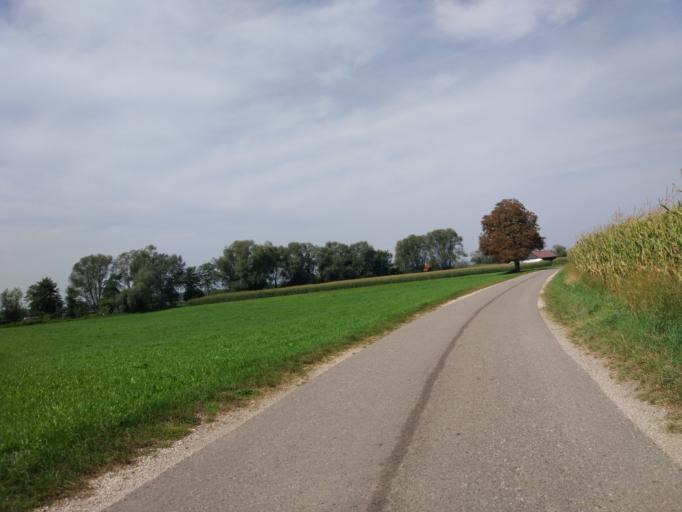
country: DE
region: Baden-Wuerttemberg
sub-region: Tuebingen Region
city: Achstetten
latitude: 48.2820
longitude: 9.8986
